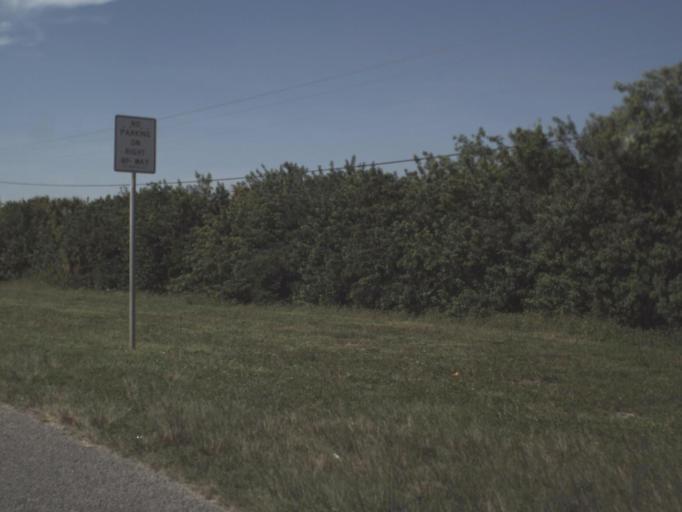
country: US
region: Florida
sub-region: Glades County
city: Moore Haven
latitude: 26.8340
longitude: -81.1190
